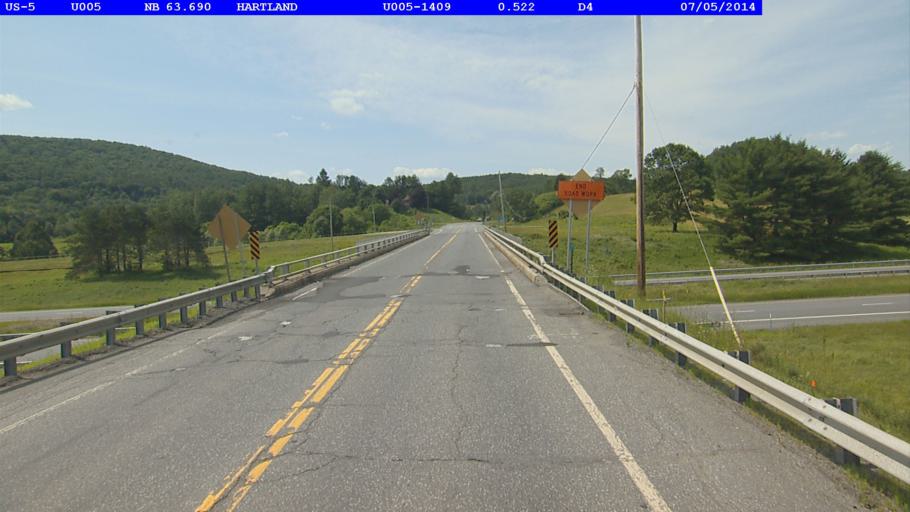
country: US
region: Vermont
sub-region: Windsor County
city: Windsor
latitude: 43.5270
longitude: -72.4016
